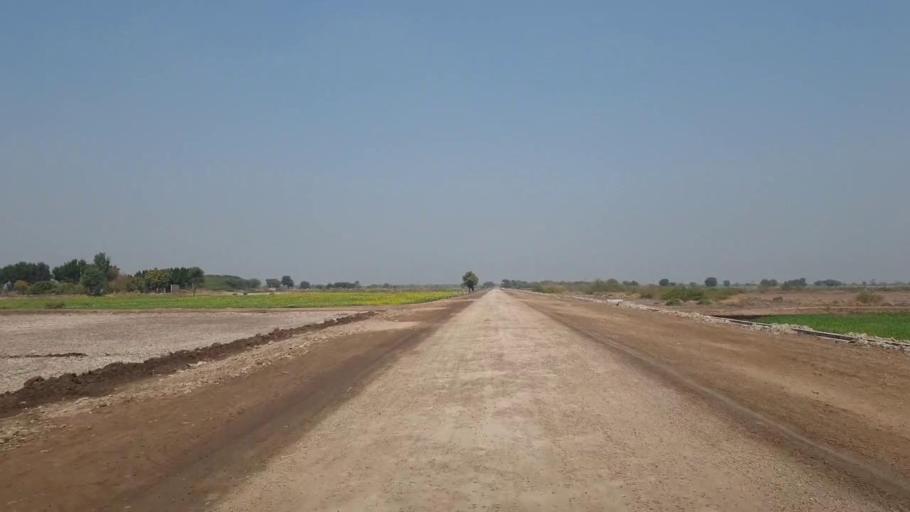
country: PK
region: Sindh
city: Mirwah Gorchani
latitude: 25.3672
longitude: 68.9316
